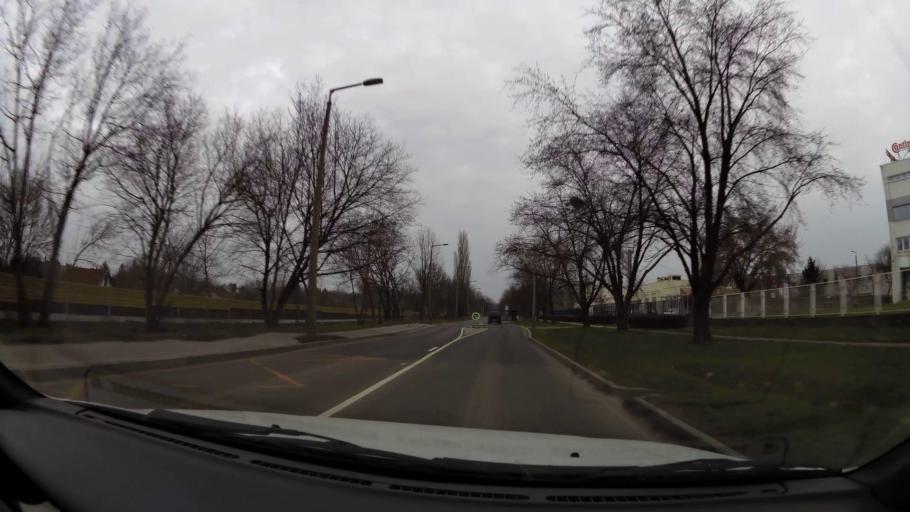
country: HU
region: Budapest
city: Budapest X. keruelet
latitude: 47.4823
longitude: 19.2034
